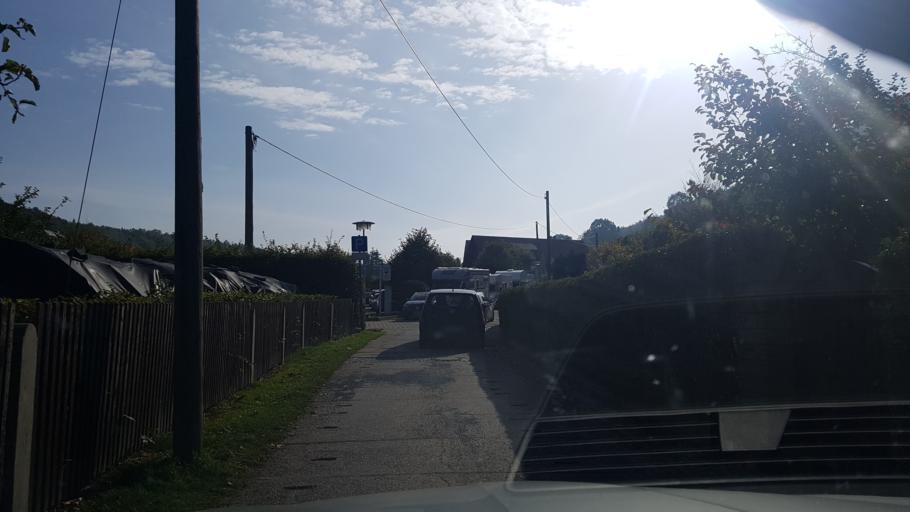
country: DE
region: Saxony
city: Konigstein
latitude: 50.9067
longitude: 14.0810
